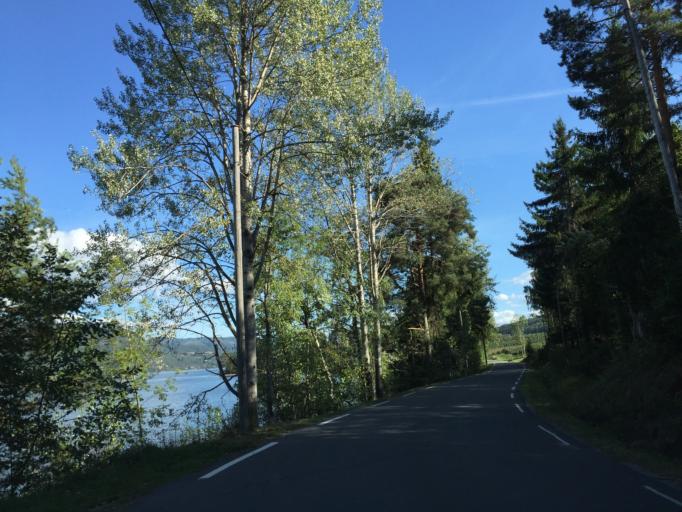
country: NO
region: Buskerud
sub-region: Ovre Eiker
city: Hokksund
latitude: 59.6775
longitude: 9.8656
